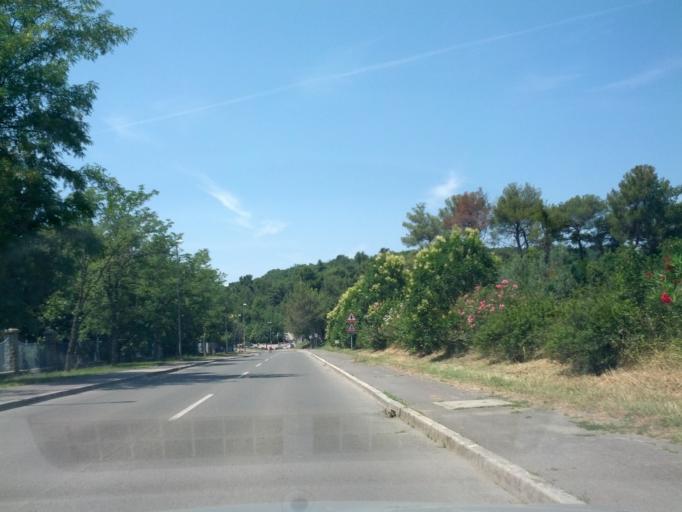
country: SI
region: Koper-Capodistria
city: Ankaran
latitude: 45.5811
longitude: 13.7297
